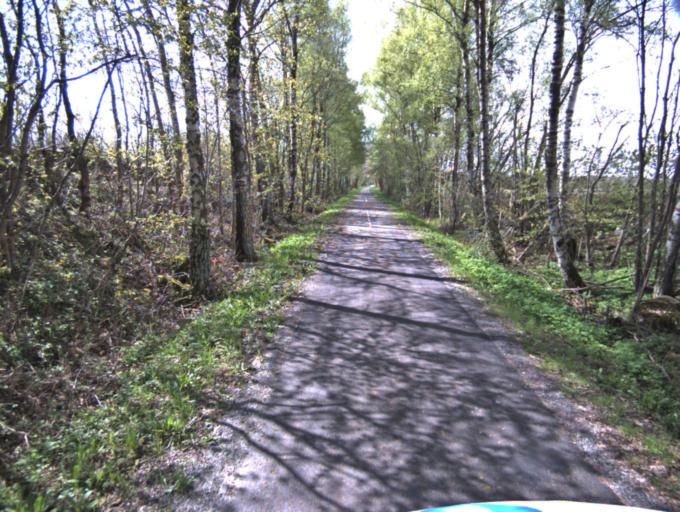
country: SE
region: Skane
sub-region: Kristianstads Kommun
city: Onnestad
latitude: 56.0040
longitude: 14.0481
